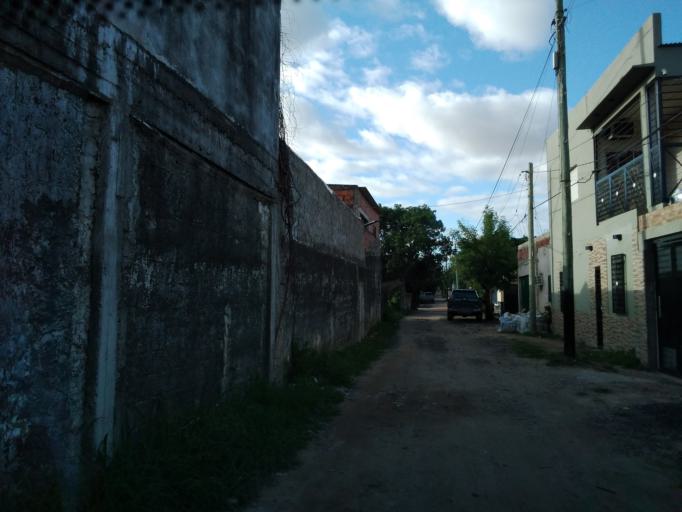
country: AR
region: Corrientes
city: Corrientes
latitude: -27.4779
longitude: -58.8084
